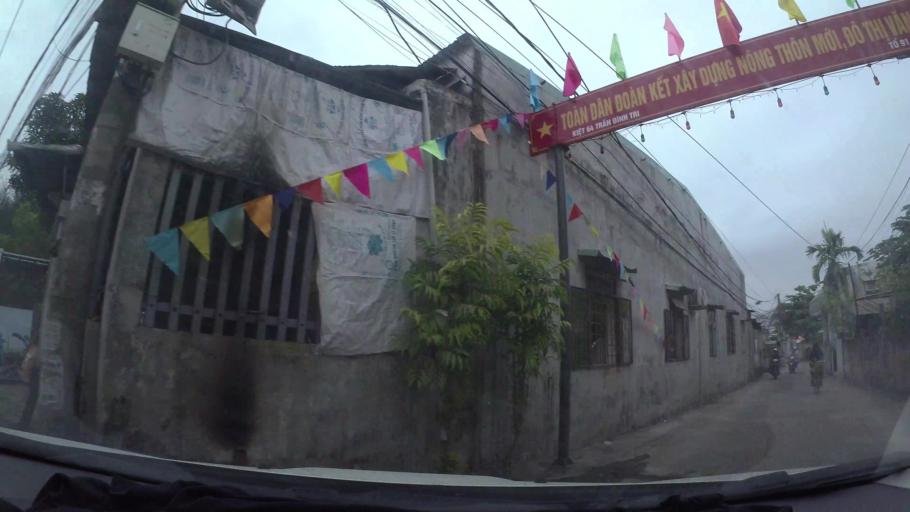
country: VN
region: Da Nang
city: Lien Chieu
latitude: 16.0836
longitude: 108.1557
